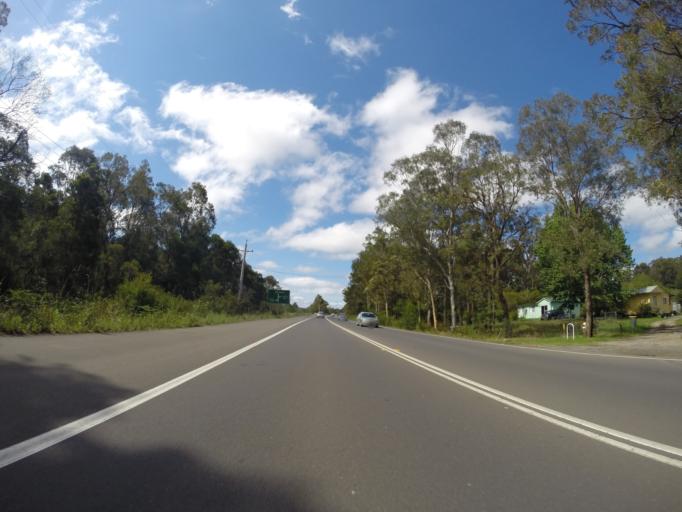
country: AU
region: New South Wales
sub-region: Shoalhaven Shire
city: Falls Creek
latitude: -34.9883
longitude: 150.5860
